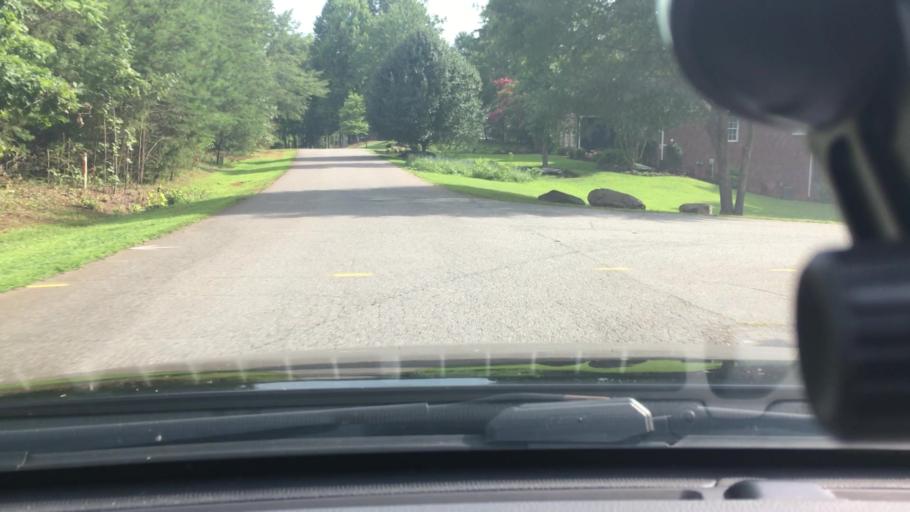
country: US
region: North Carolina
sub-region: Rutherford County
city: Rutherfordton
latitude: 35.3866
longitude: -81.9736
